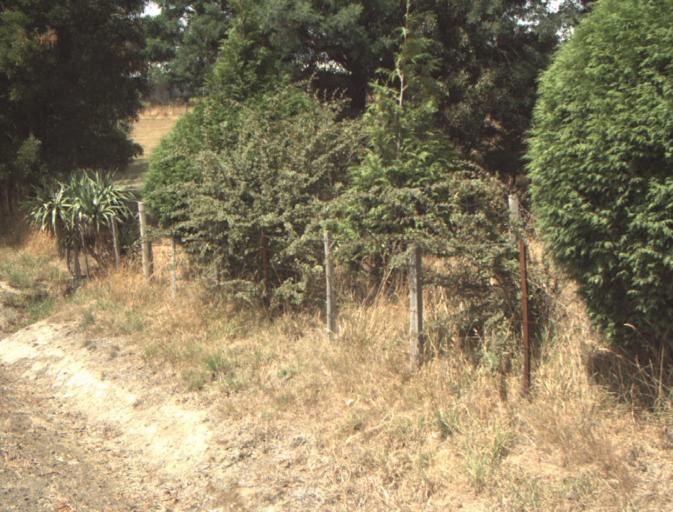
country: AU
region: Tasmania
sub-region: Launceston
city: Mayfield
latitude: -41.2361
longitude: 147.1251
